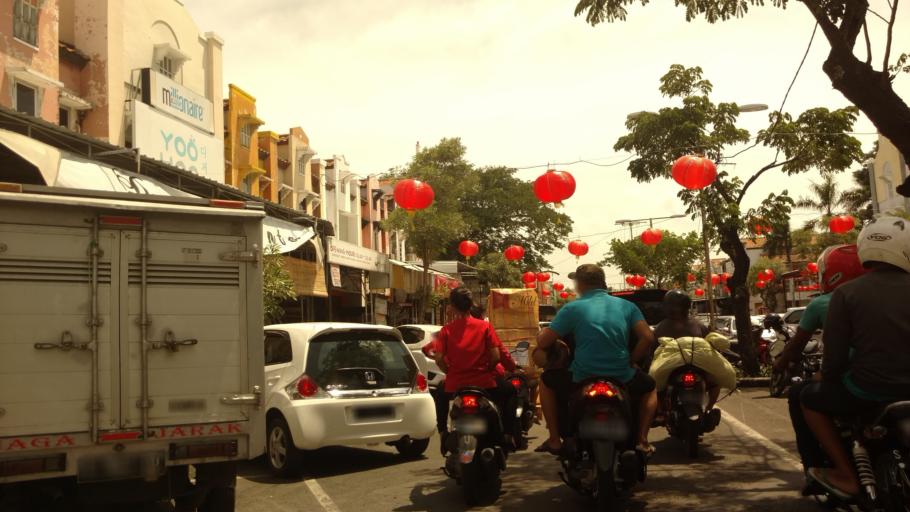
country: ID
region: East Java
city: Driyorejo
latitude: -7.2873
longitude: 112.6557
